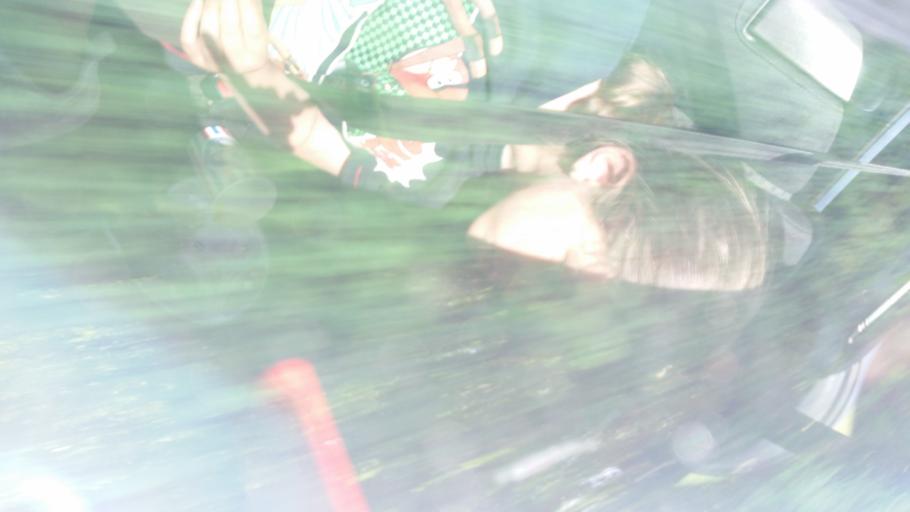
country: IE
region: Leinster
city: Lusk
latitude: 53.5087
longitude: -6.2095
